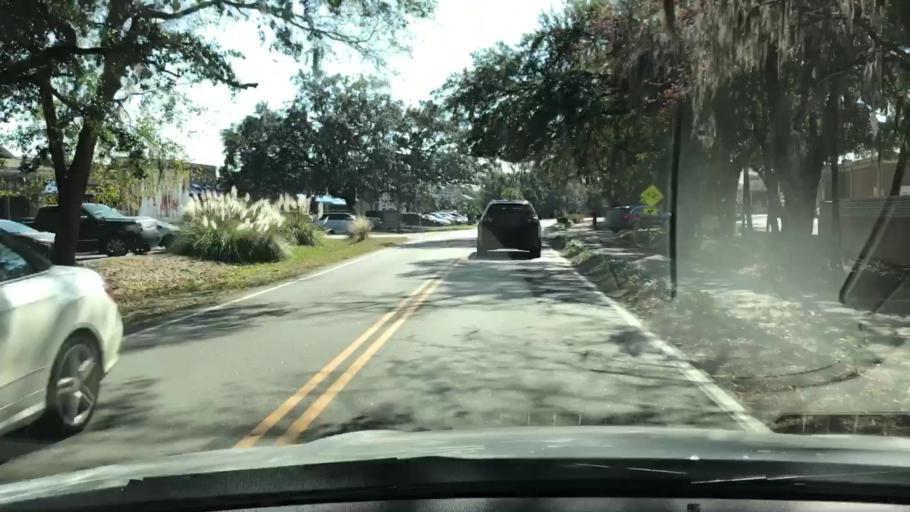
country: US
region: South Carolina
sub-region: Beaufort County
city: Hilton Head Island
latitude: 32.2192
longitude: -80.7038
